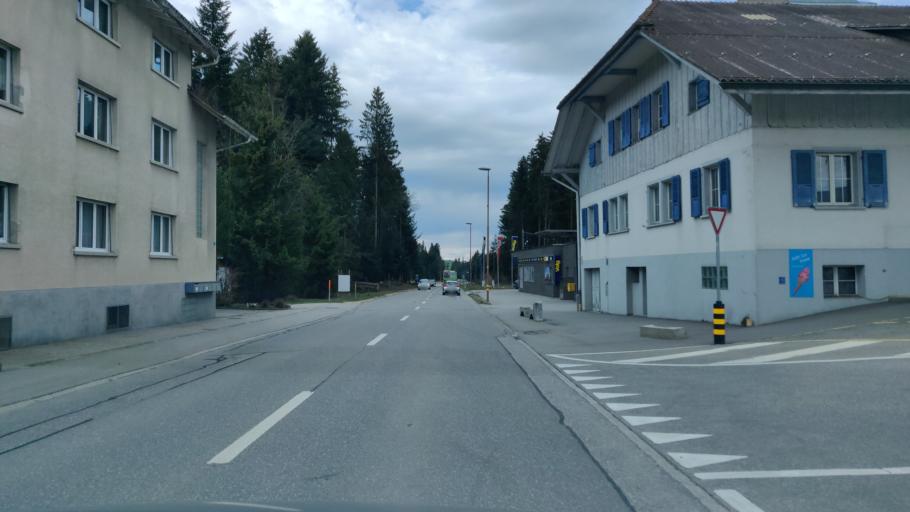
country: CH
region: Bern
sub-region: Emmental District
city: Sumiswald
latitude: 47.0627
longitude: 7.7495
